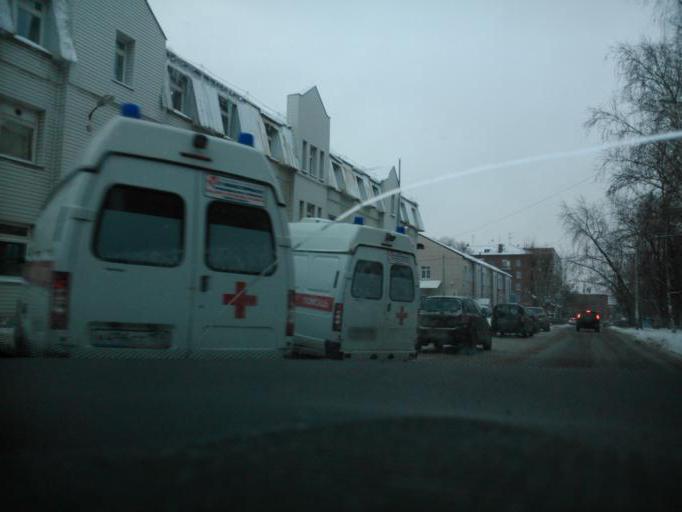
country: RU
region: Perm
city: Perm
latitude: 57.9880
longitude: 56.2511
